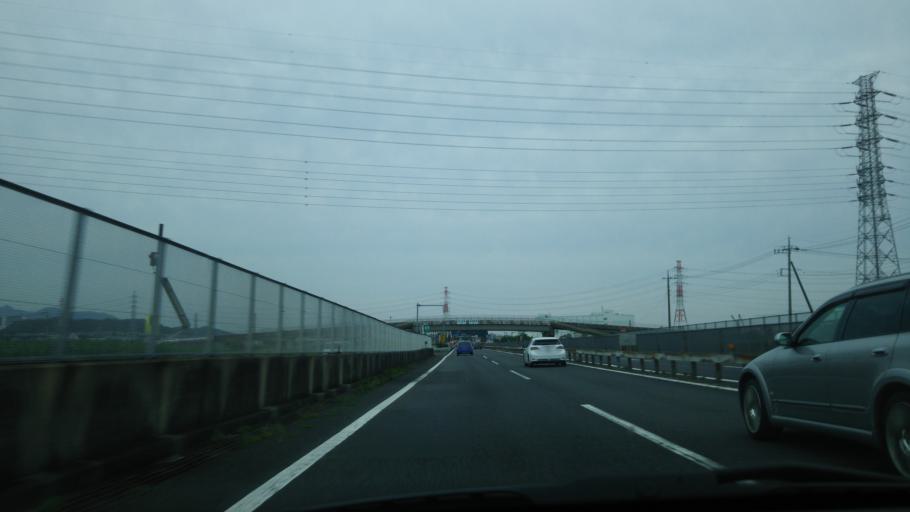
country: JP
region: Kanagawa
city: Isehara
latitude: 35.3962
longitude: 139.3346
